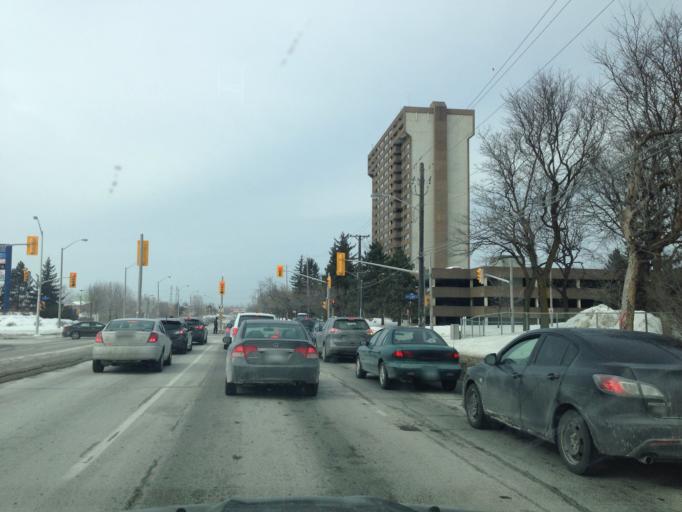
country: CA
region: Ontario
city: Ottawa
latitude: 45.3553
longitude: -75.6505
